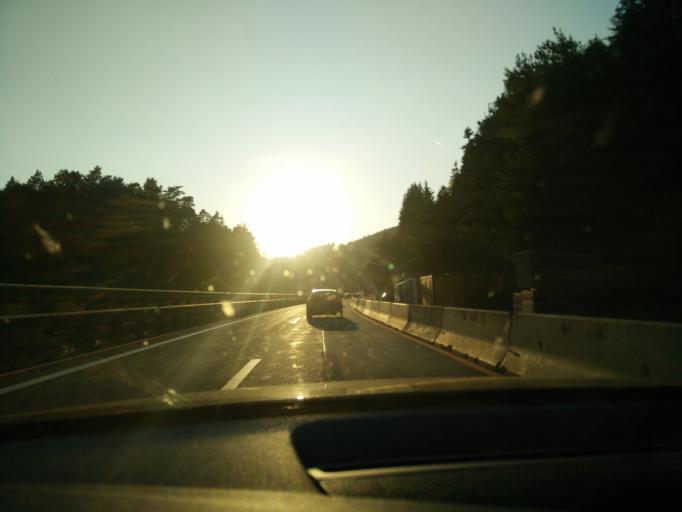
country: AT
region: Carinthia
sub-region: Politischer Bezirk Villach Land
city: Velden am Woerthersee
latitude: 46.6232
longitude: 14.0619
